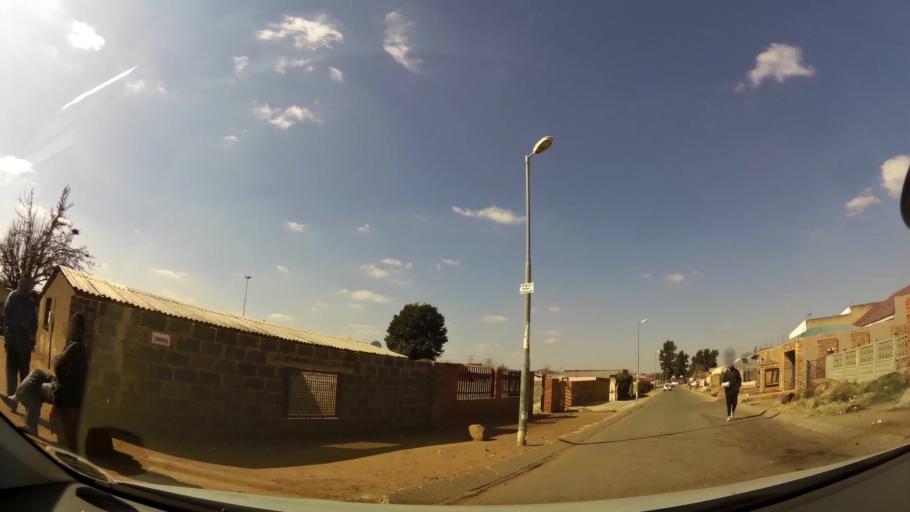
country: ZA
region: Gauteng
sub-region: City of Johannesburg Metropolitan Municipality
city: Soweto
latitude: -26.2477
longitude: 27.8856
